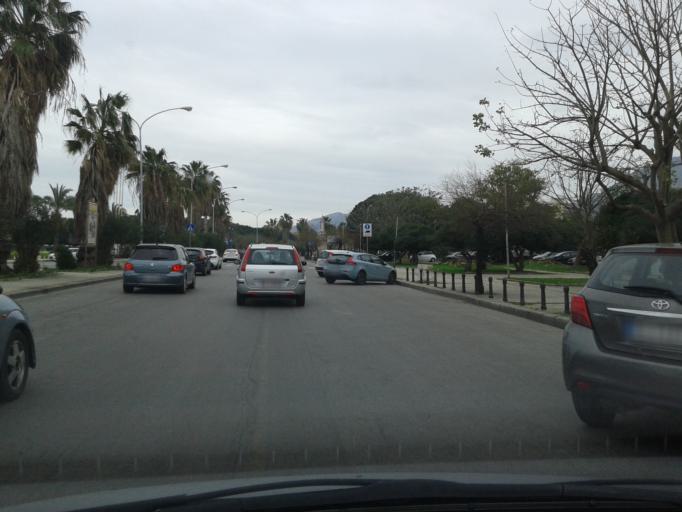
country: IT
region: Sicily
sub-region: Palermo
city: Palermo
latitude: 38.1160
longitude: 13.3750
